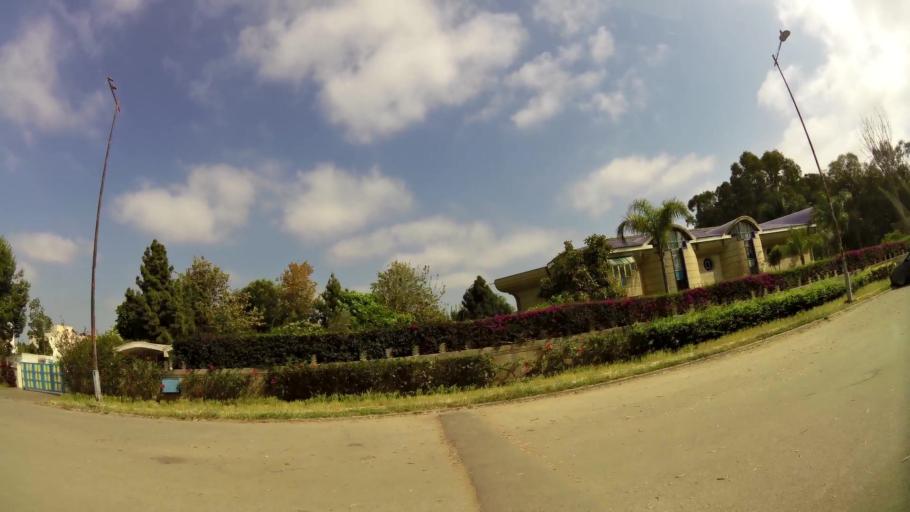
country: MA
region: Rabat-Sale-Zemmour-Zaer
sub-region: Rabat
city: Rabat
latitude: 33.9859
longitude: -6.8403
